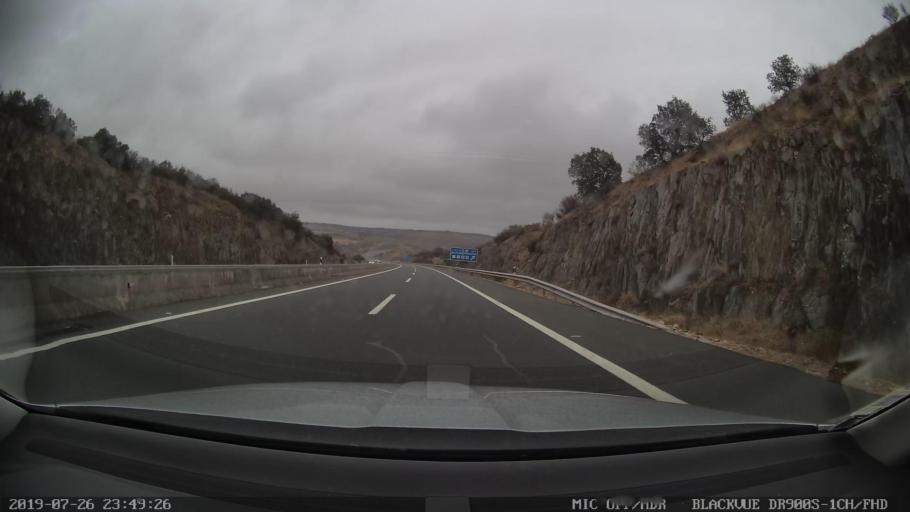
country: ES
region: Extremadura
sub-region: Provincia de Caceres
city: Jaraicejo
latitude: 39.6415
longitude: -5.8089
